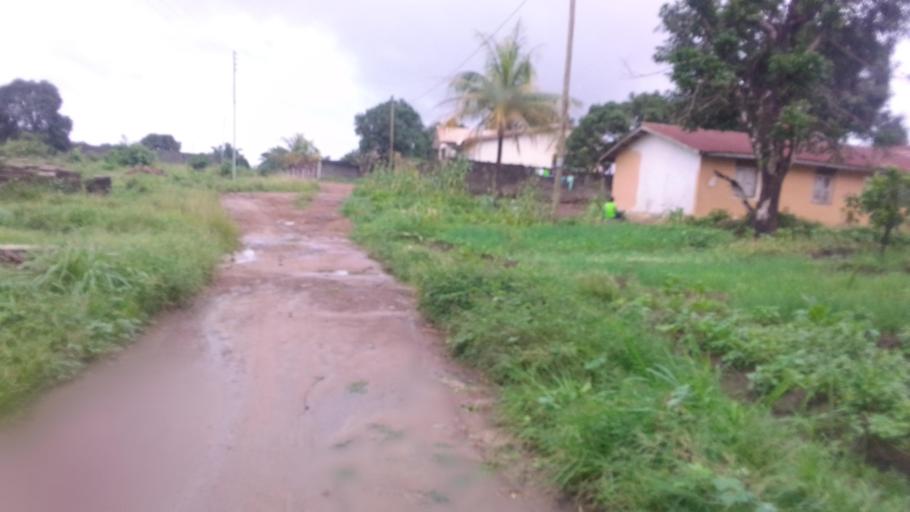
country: SL
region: Eastern Province
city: Kenema
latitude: 7.8878
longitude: -11.1726
